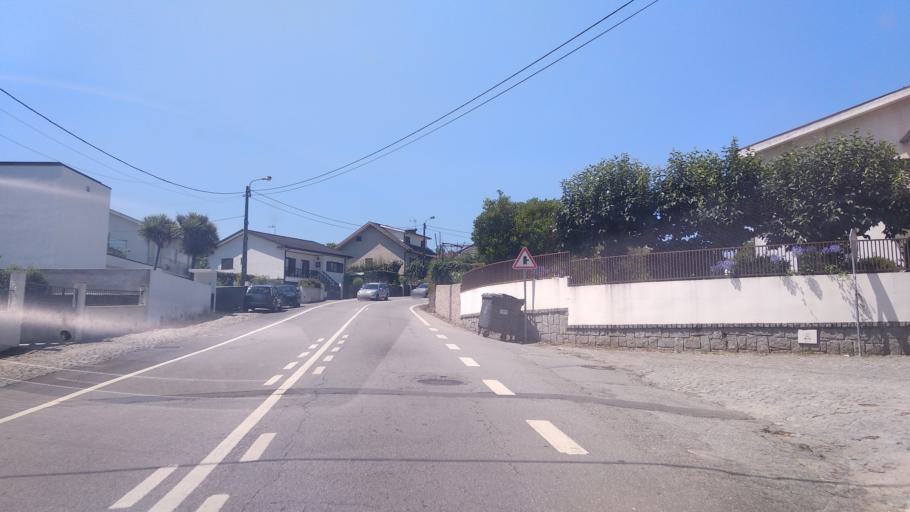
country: PT
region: Braga
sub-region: Braga
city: Braga
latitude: 41.5728
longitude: -8.4203
